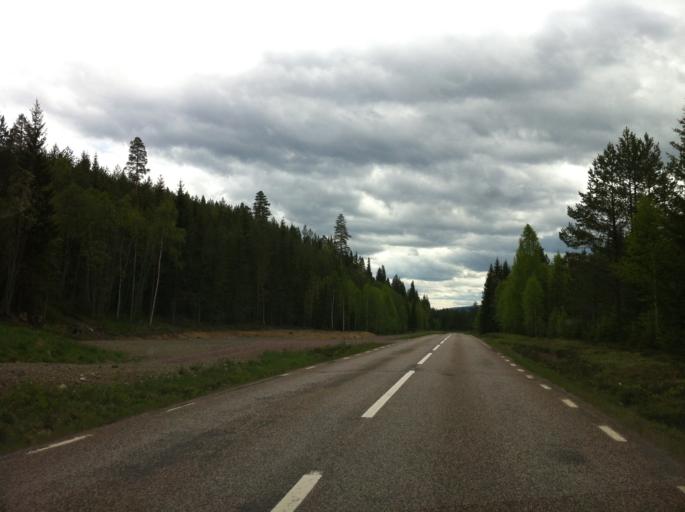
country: SE
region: Dalarna
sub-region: Malung-Saelens kommun
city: Malung
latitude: 61.2591
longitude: 13.1926
